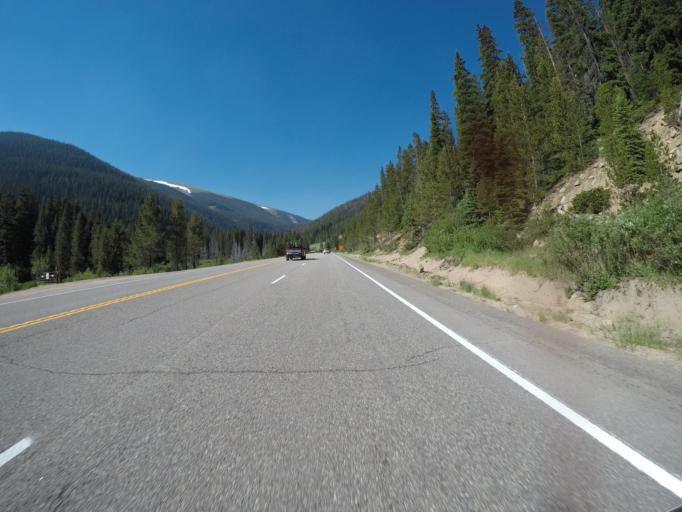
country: US
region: Colorado
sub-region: Grand County
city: Fraser
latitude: 39.8328
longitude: -105.7575
